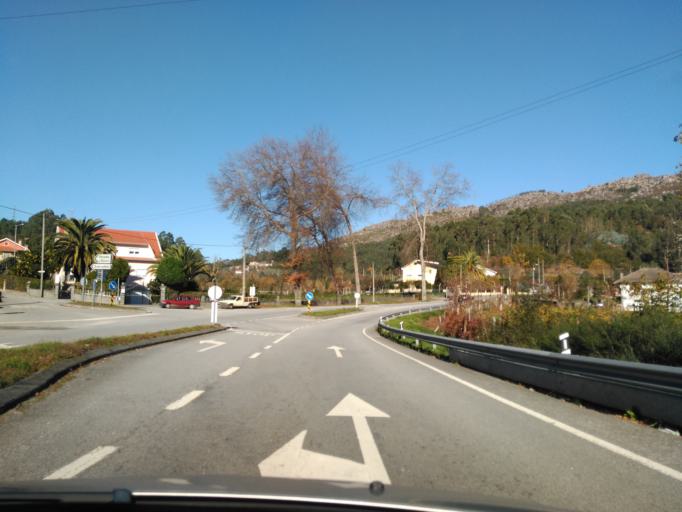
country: PT
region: Braga
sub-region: Povoa de Lanhoso
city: Povoa de Lanhoso
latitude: 41.6140
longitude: -8.2566
